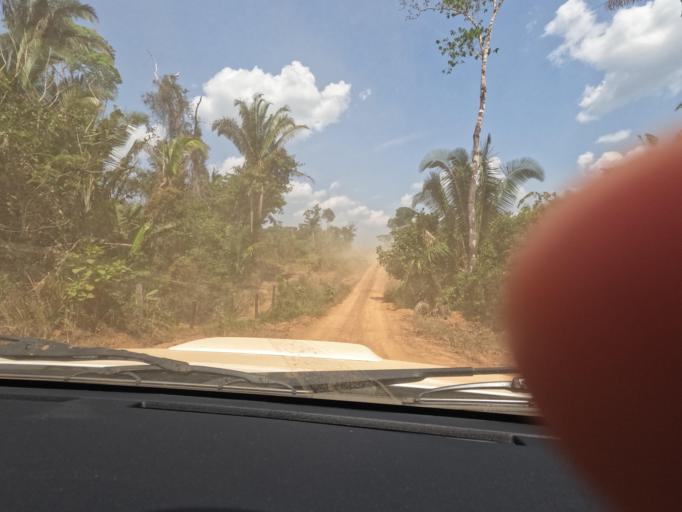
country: BR
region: Rondonia
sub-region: Porto Velho
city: Porto Velho
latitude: -8.6096
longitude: -64.2225
